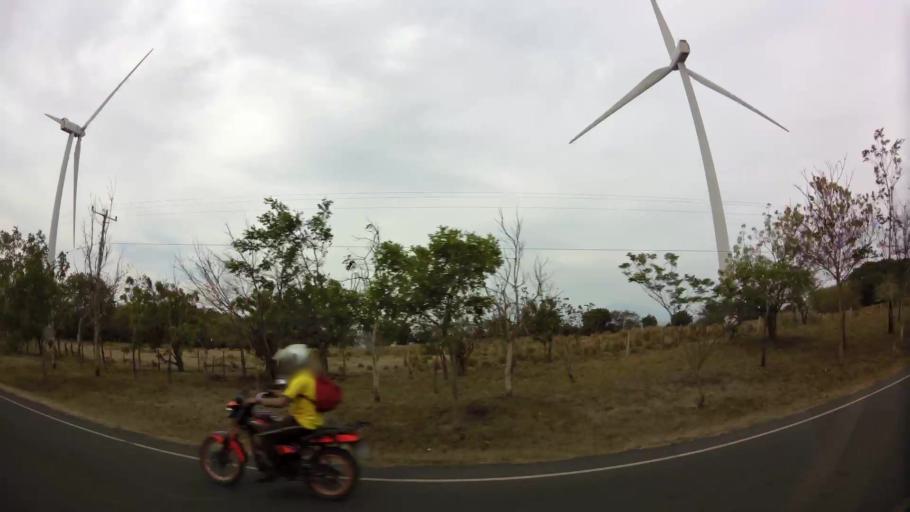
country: NI
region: Rivas
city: Rivas
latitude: 11.3521
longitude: -85.7397
